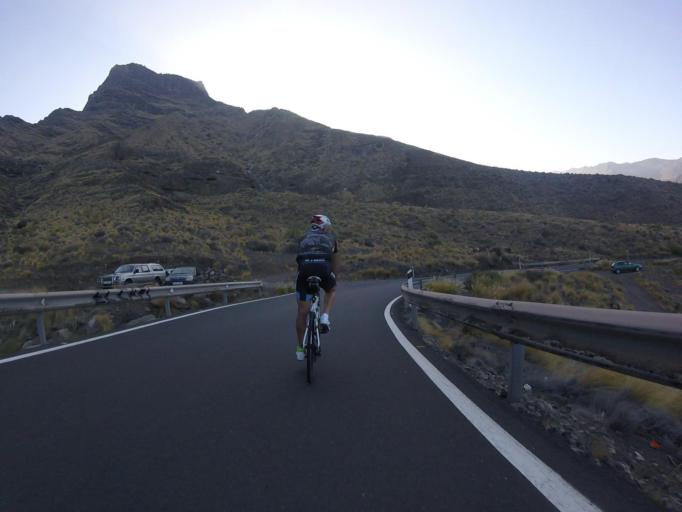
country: ES
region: Canary Islands
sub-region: Provincia de Las Palmas
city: Agaete
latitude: 28.0600
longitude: -15.7298
